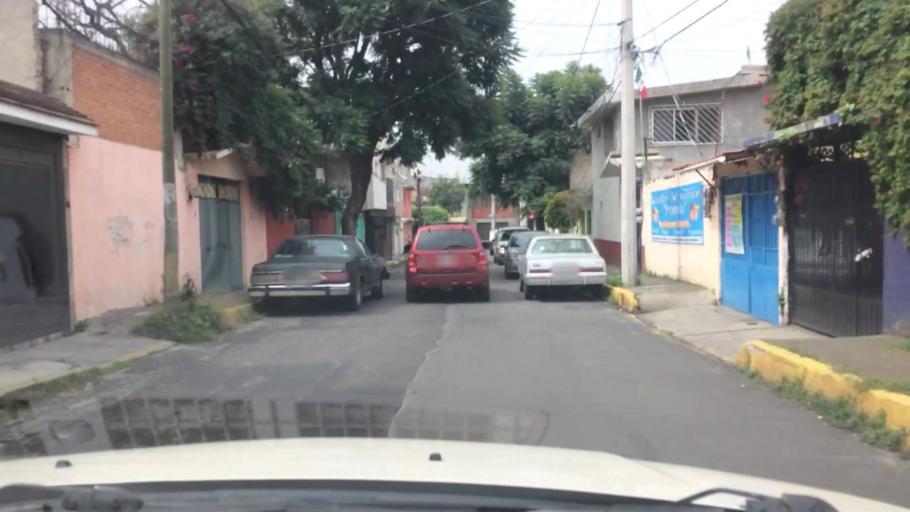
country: MX
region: Mexico City
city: Xochimilco
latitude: 19.2659
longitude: -99.1309
